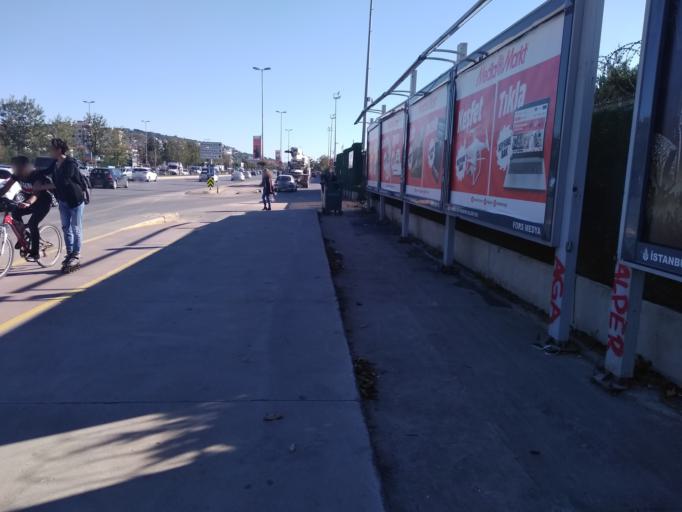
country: TR
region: Istanbul
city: Maltepe
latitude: 40.9190
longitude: 29.1289
